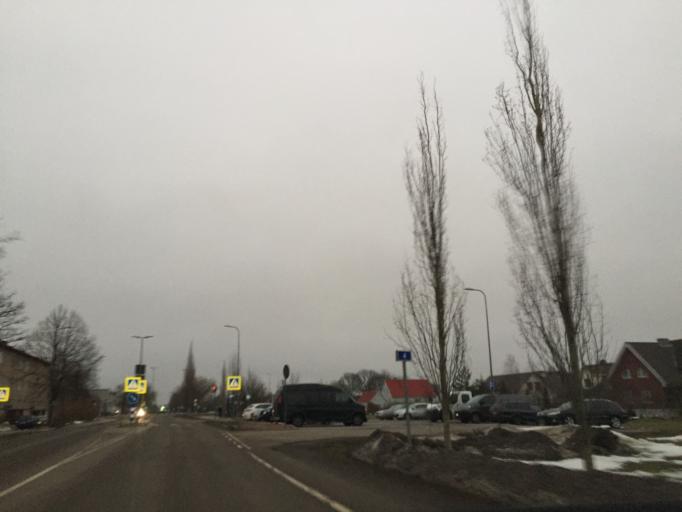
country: EE
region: Saare
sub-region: Kuressaare linn
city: Kuressaare
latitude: 58.2532
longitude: 22.5095
